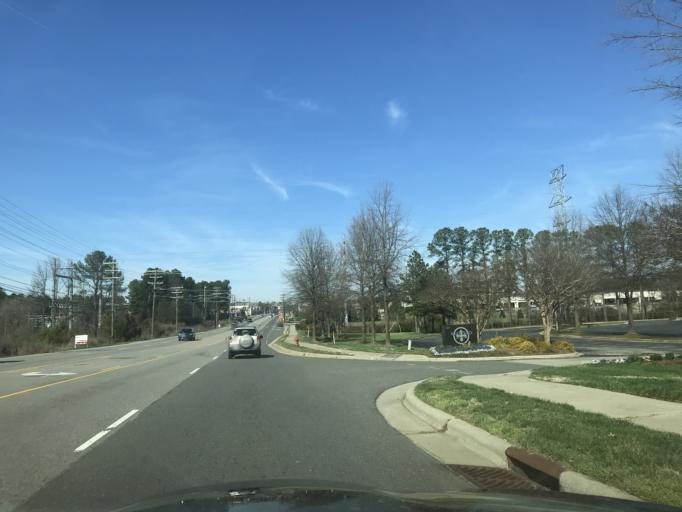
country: US
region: North Carolina
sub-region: Wake County
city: Morrisville
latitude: 35.8716
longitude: -78.8509
